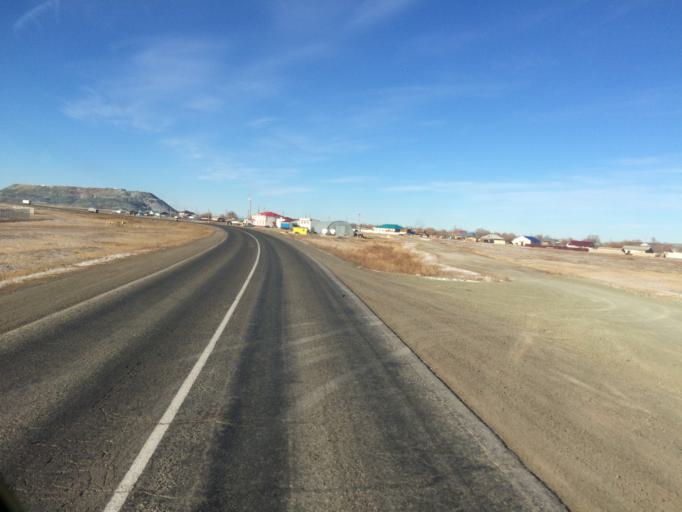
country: KZ
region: Aqtoebe
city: Khromtau
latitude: 50.2498
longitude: 58.5036
